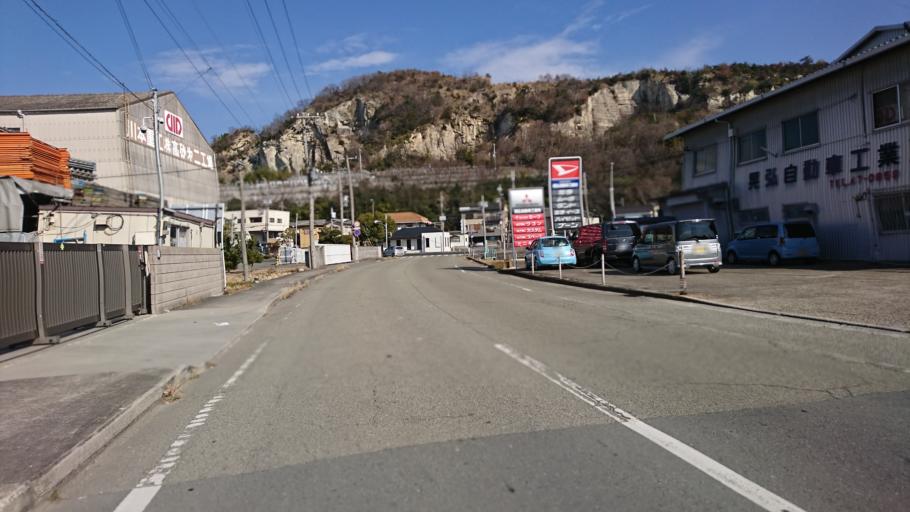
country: JP
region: Hyogo
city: Kakogawacho-honmachi
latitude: 34.7795
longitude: 134.7884
